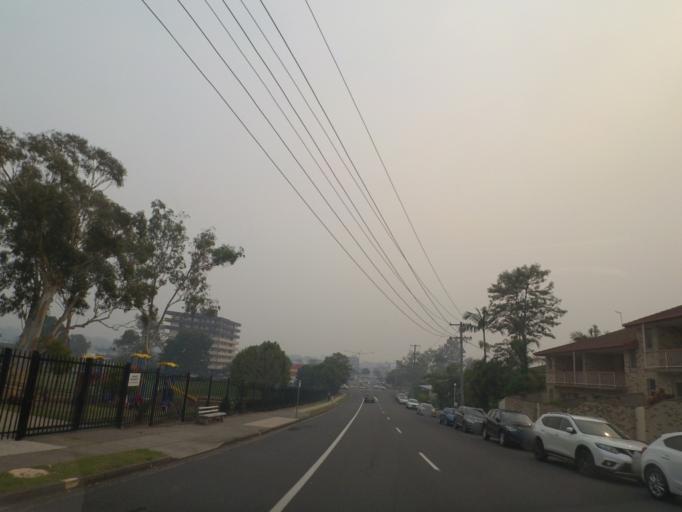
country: AU
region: New South Wales
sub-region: Coffs Harbour
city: Coffs Harbour
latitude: -30.3007
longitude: 153.1137
